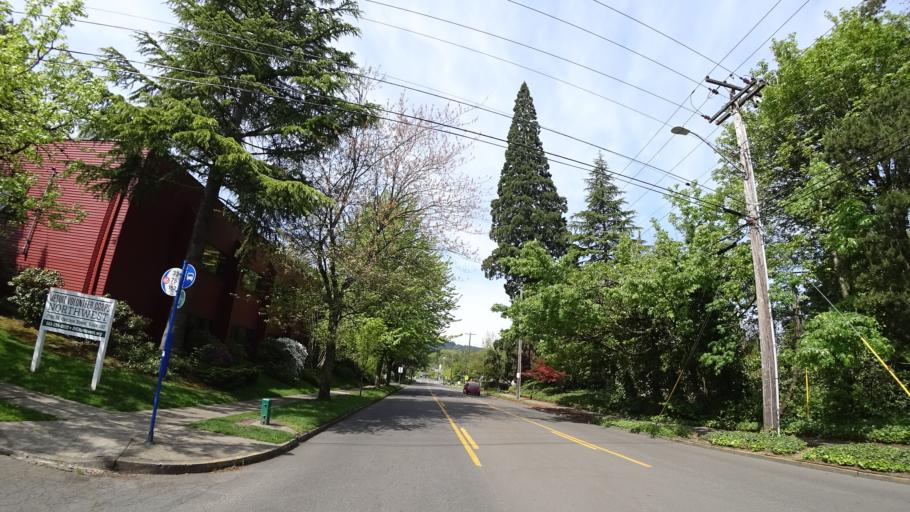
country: US
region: Oregon
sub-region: Clackamas County
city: Milwaukie
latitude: 45.4465
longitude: -122.6349
